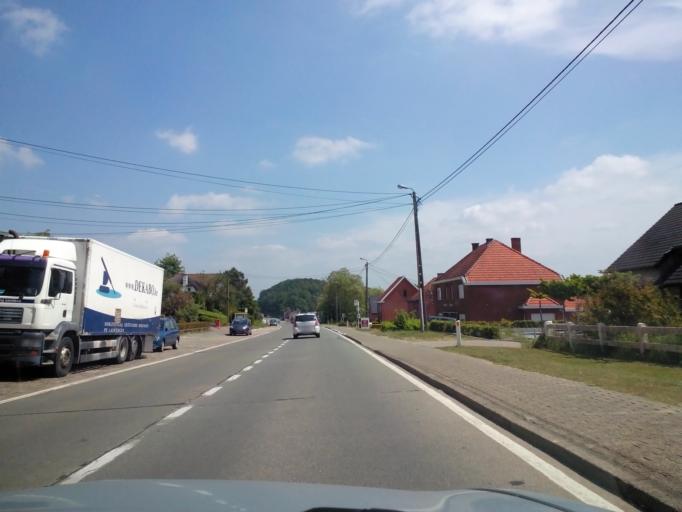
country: BE
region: Flanders
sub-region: Provincie Vlaams-Brabant
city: Holsbeek
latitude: 50.9638
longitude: 4.7840
